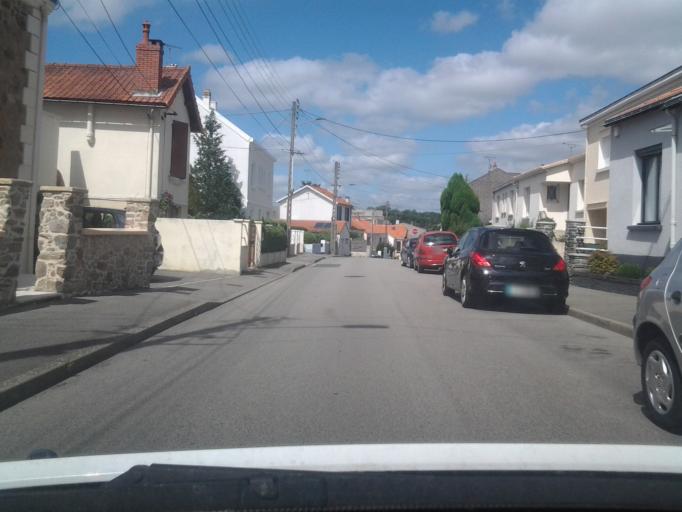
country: FR
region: Pays de la Loire
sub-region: Departement de la Vendee
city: La Roche-sur-Yon
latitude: 46.6619
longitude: -1.4330
